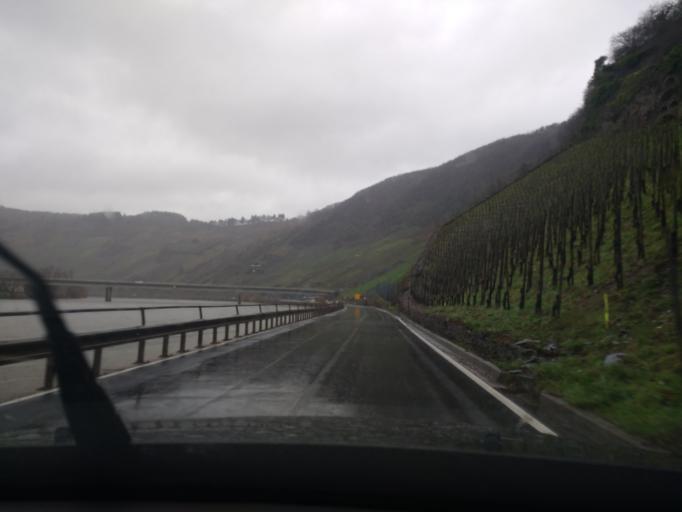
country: DE
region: Rheinland-Pfalz
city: Enkirch
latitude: 49.9742
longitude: 7.1083
